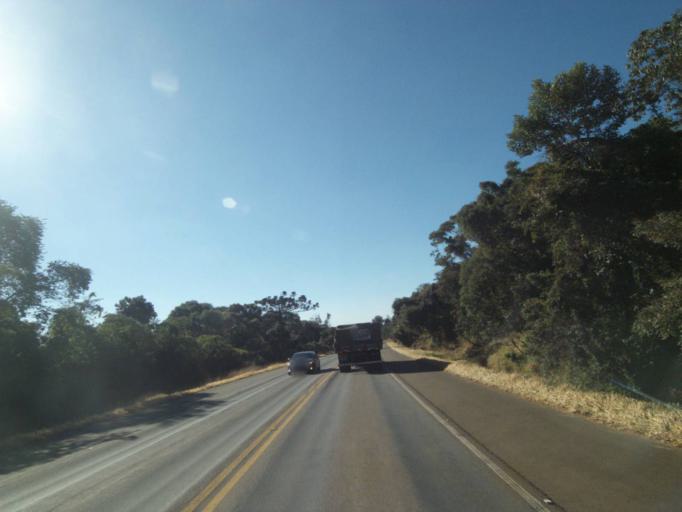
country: BR
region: Parana
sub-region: Tibagi
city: Tibagi
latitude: -24.6673
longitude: -50.4528
